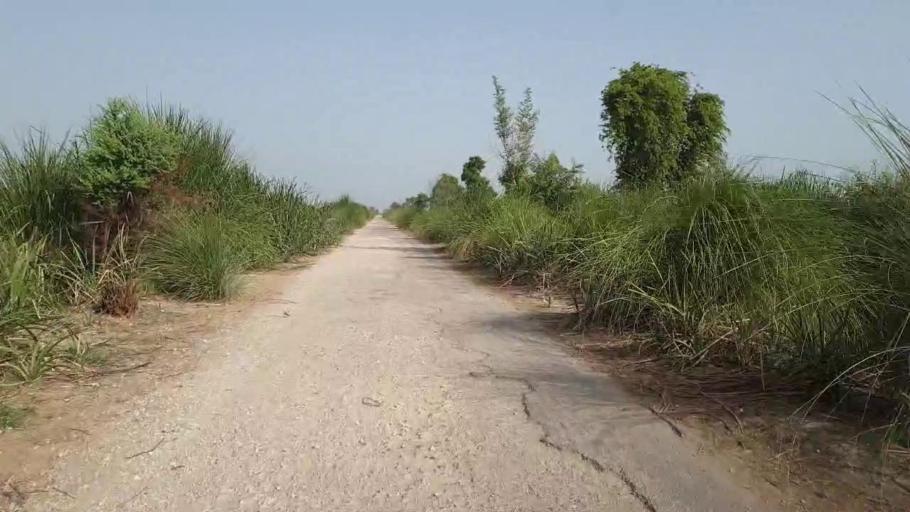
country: PK
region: Sindh
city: Daur
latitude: 26.3450
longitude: 68.1783
